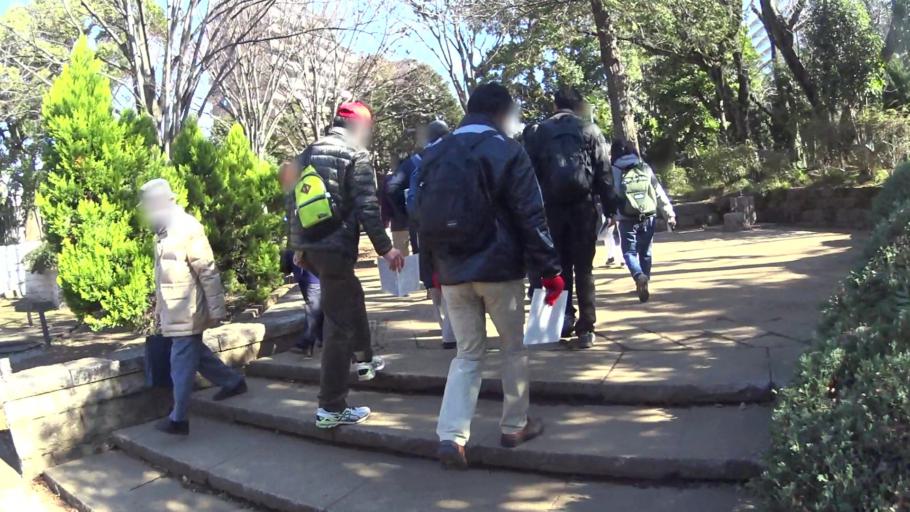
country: JP
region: Saitama
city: Yono
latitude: 35.8622
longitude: 139.6508
